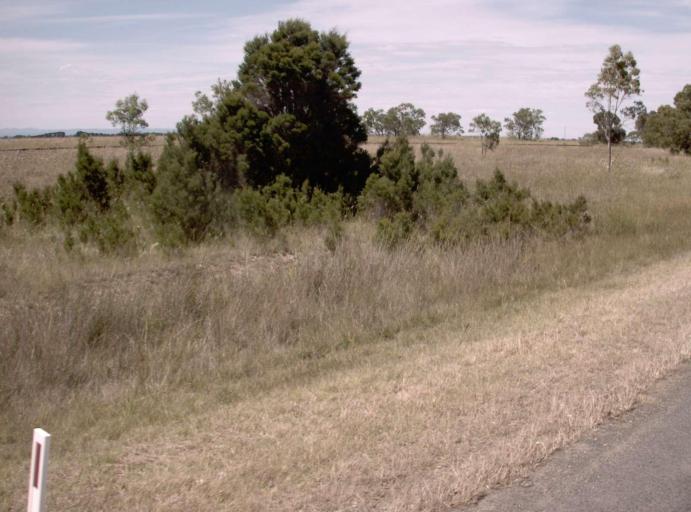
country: AU
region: Victoria
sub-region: Wellington
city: Sale
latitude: -38.1031
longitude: 146.9341
